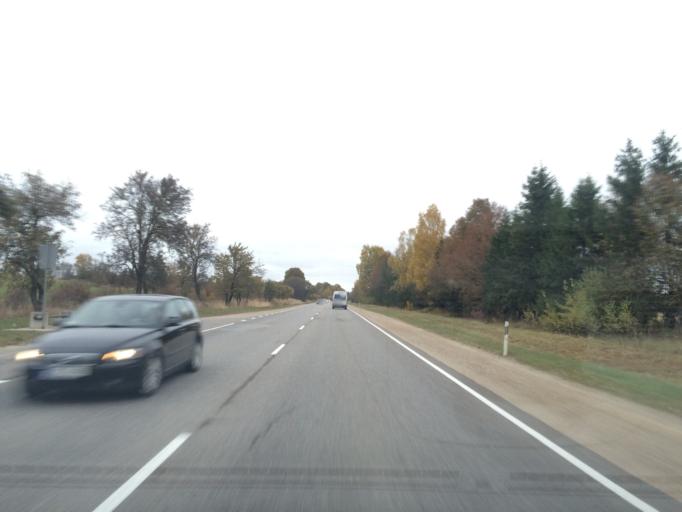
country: LV
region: Plavinu
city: Plavinas
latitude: 56.5911
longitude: 25.6168
